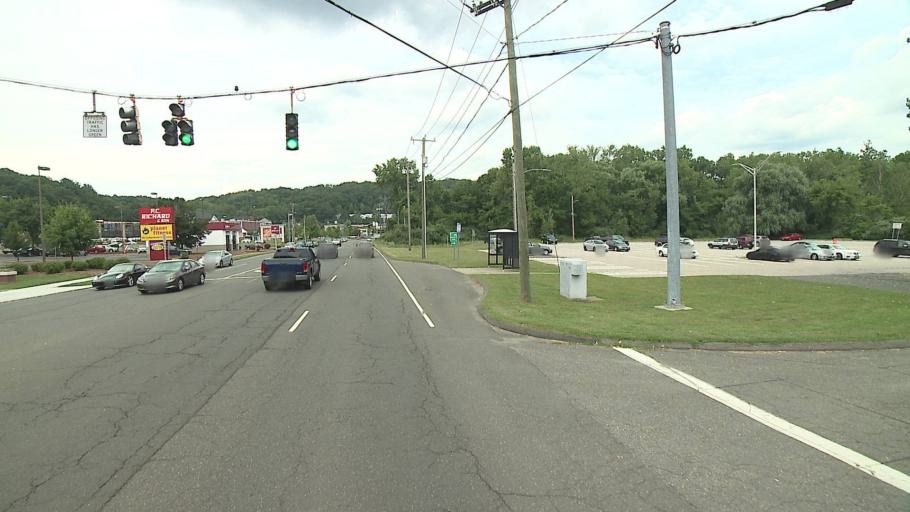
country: US
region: Connecticut
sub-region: Fairfield County
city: Danbury
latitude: 41.4226
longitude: -73.4198
